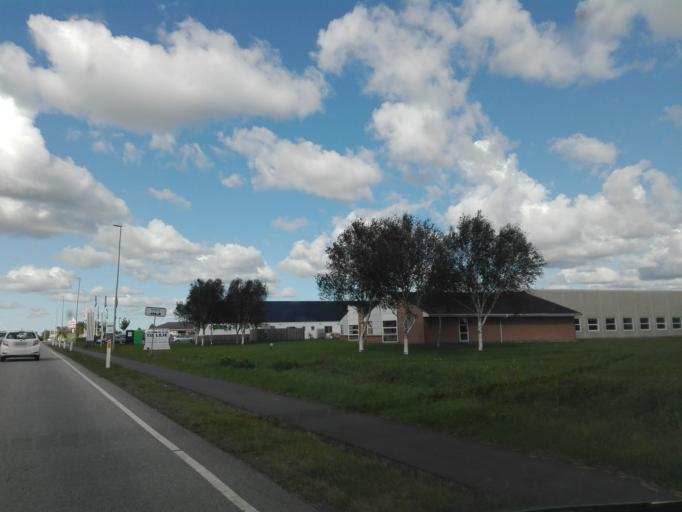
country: DK
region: North Denmark
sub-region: Mariagerfjord Kommune
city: Hobro
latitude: 56.6248
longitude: 9.8051
